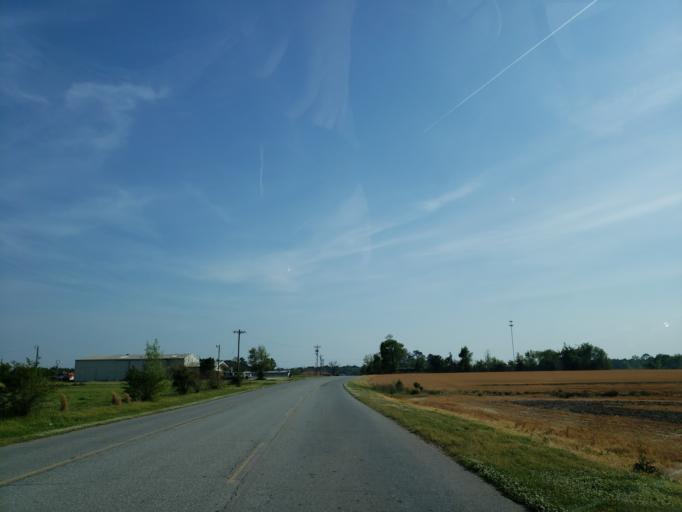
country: US
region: Georgia
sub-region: Dooly County
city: Vienna
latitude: 32.0900
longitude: -83.7674
